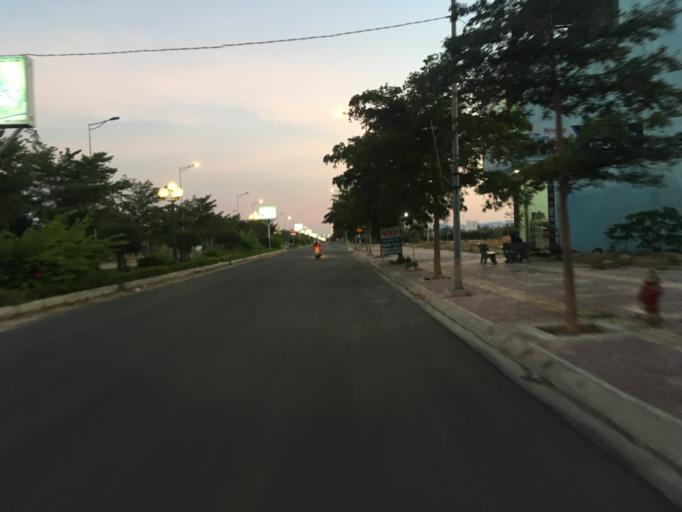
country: VN
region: Ninh Thuan
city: Phan Rang-Thap Cham
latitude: 11.5774
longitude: 109.0009
